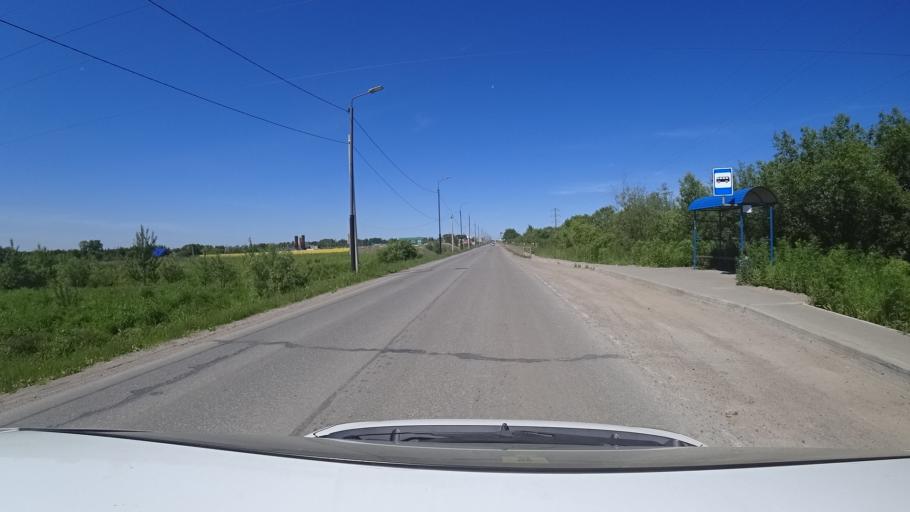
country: RU
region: Khabarovsk Krai
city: Topolevo
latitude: 48.4883
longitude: 135.1836
